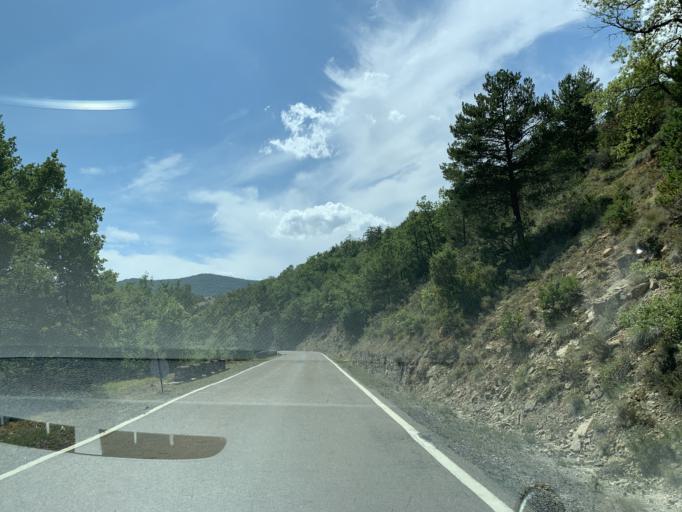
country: ES
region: Aragon
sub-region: Provincia de Huesca
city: Jasa
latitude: 42.6242
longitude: -0.6559
